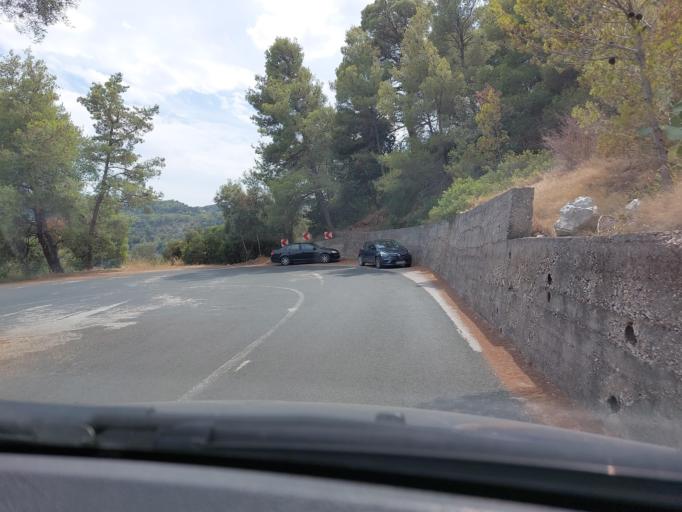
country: HR
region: Dubrovacko-Neretvanska
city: Smokvica
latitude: 42.7648
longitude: 16.8916
